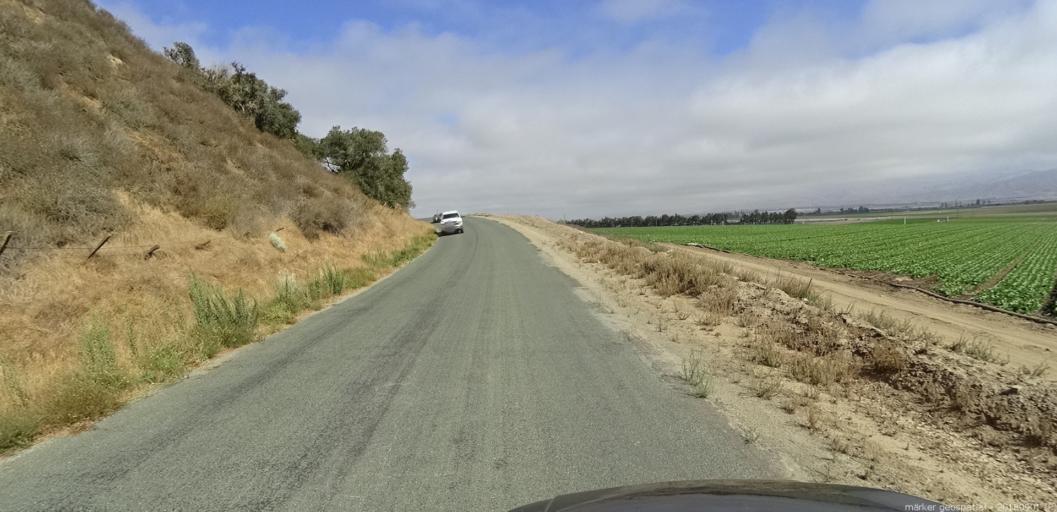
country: US
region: California
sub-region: Monterey County
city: Soledad
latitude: 36.4042
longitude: -121.3803
